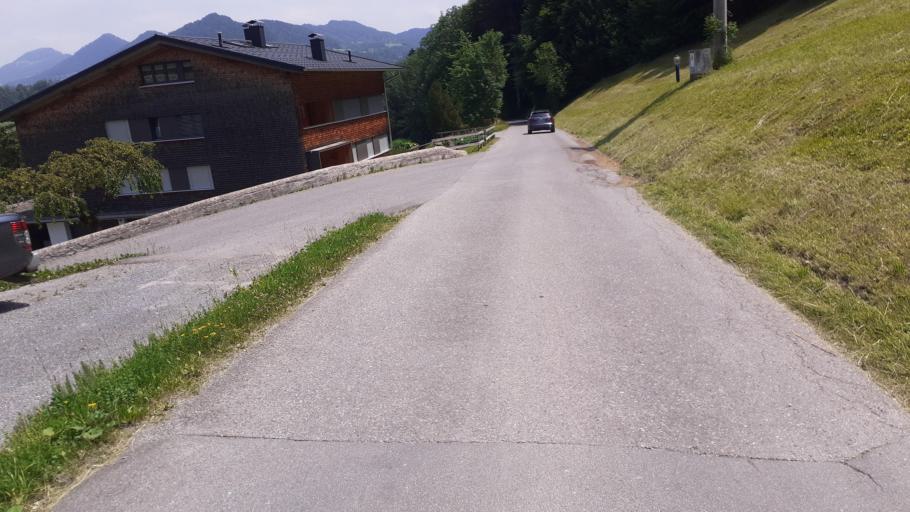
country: AT
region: Vorarlberg
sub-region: Politischer Bezirk Bregenz
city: Egg
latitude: 47.4321
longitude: 9.8851
